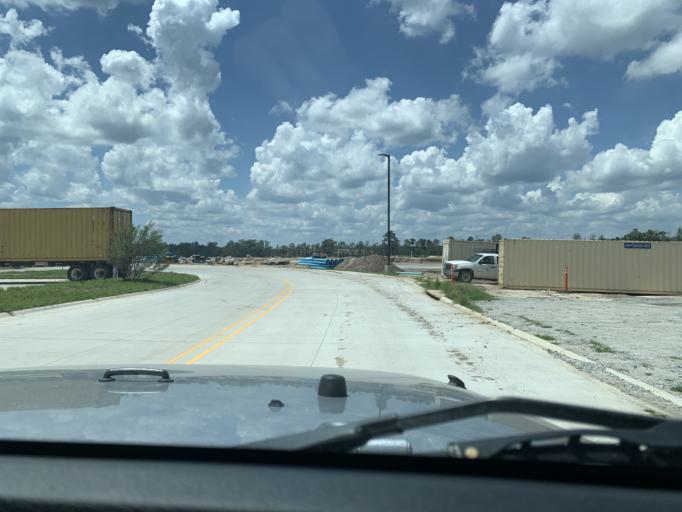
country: US
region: Georgia
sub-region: Chatham County
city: Bloomingdale
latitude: 32.1182
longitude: -81.2809
